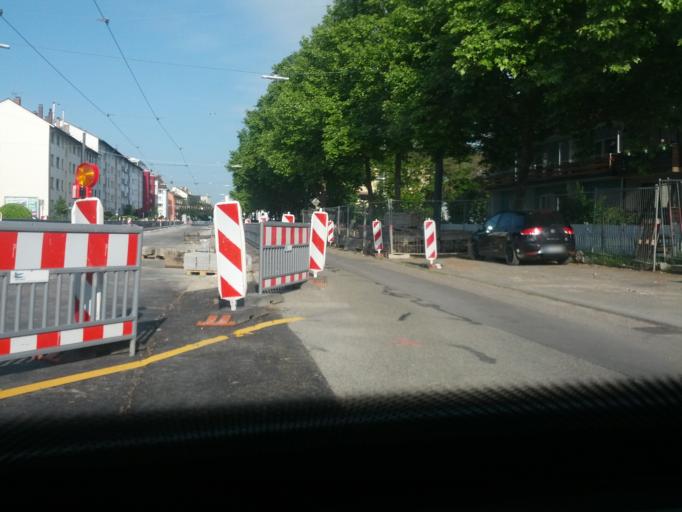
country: DE
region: Baden-Wuerttemberg
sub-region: Karlsruhe Region
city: Karlsruhe
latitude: 49.0114
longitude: 8.4354
